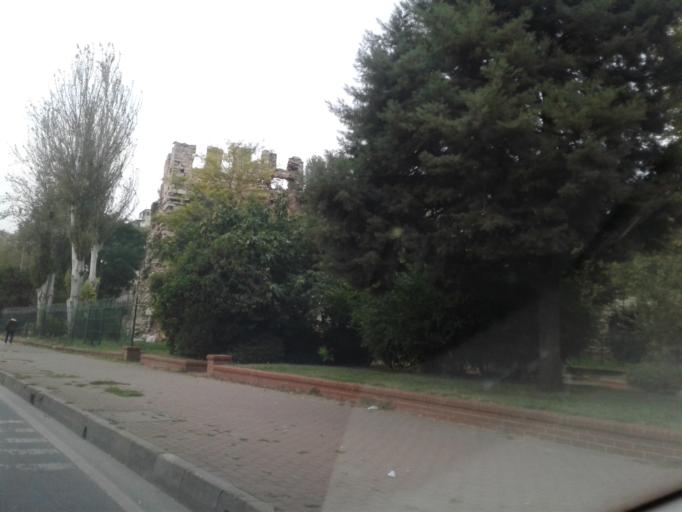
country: TR
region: Istanbul
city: Eminoenue
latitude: 41.0022
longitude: 28.9761
